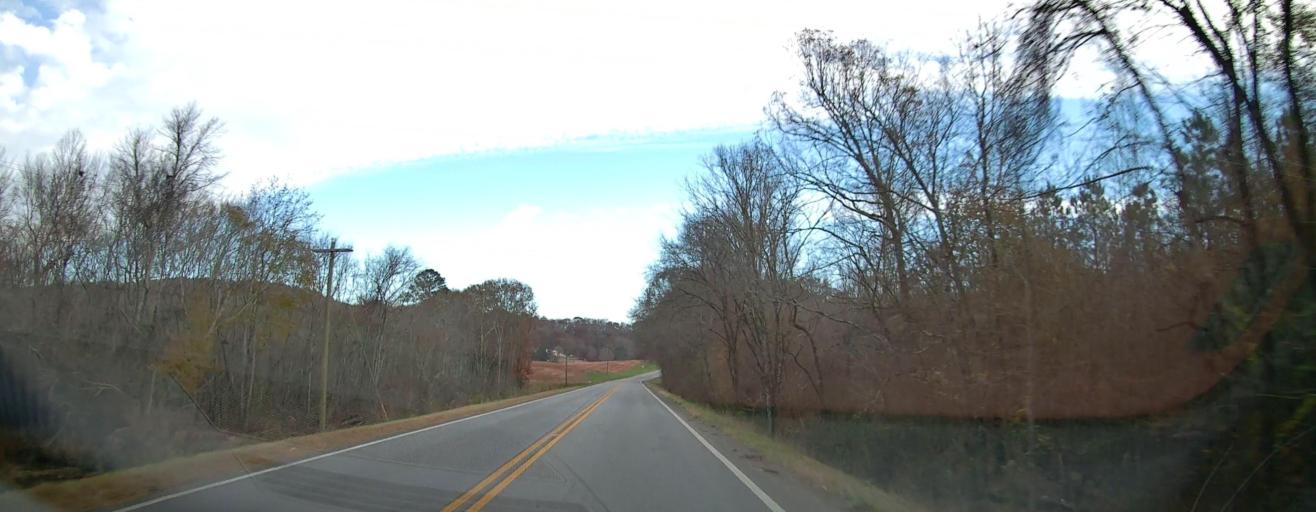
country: US
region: Alabama
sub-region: Marshall County
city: Arab
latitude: 34.3853
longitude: -86.6618
